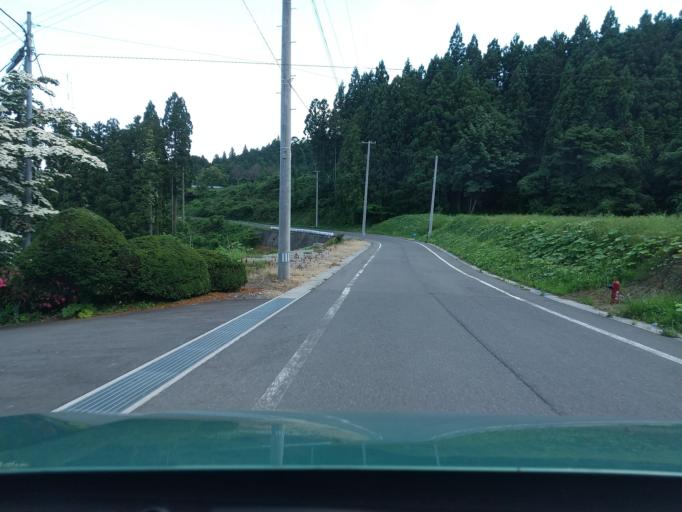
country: JP
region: Iwate
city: Ichinoseki
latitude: 38.9977
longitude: 141.2184
